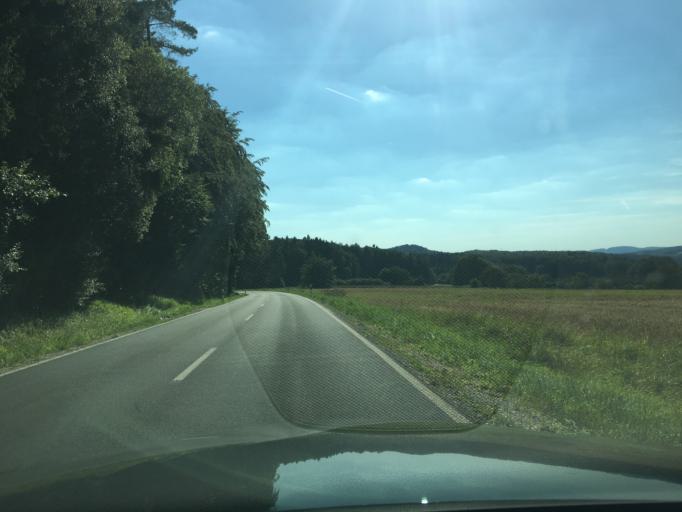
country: DE
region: Bavaria
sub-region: Upper Franconia
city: Obertrubach
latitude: 49.6870
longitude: 11.3678
